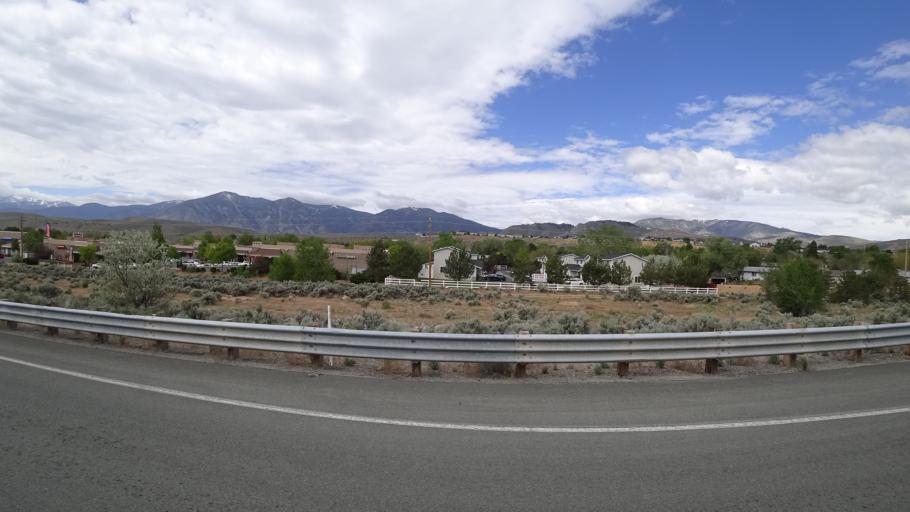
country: US
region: Nevada
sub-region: Douglas County
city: Indian Hills
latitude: 39.0930
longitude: -119.7752
